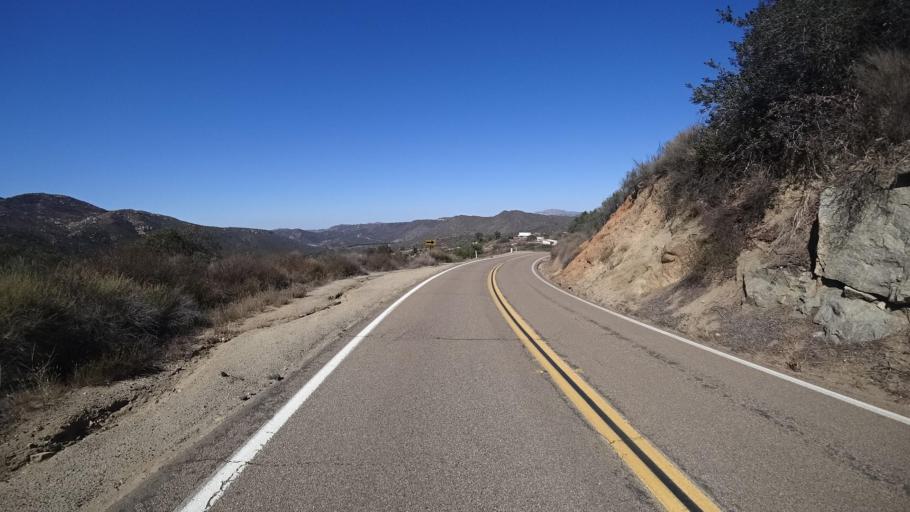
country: US
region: California
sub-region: San Diego County
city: Alpine
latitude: 32.7824
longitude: -116.7200
